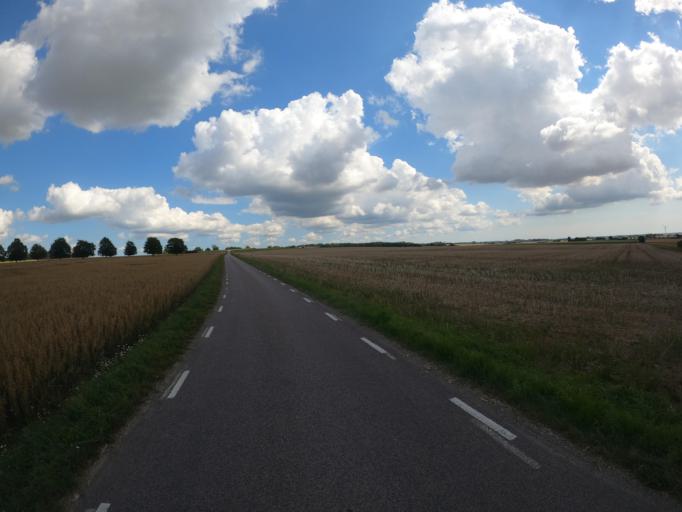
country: SE
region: Skane
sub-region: Svedala Kommun
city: Klagerup
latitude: 55.6811
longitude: 13.3039
